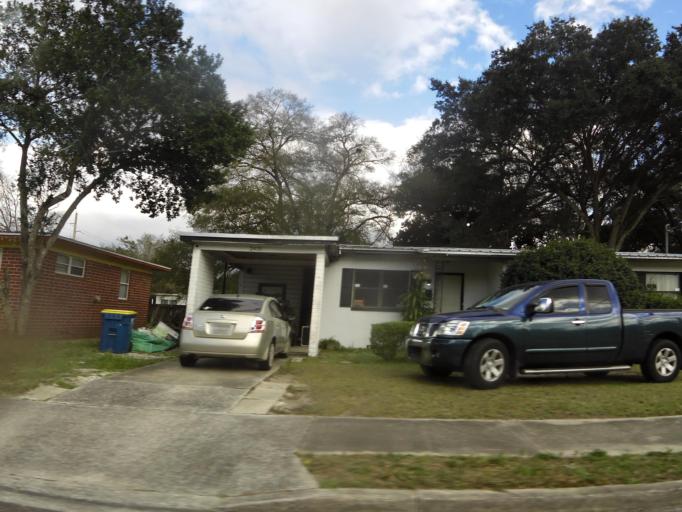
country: US
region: Florida
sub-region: Duval County
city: Jacksonville
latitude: 30.3479
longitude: -81.5893
